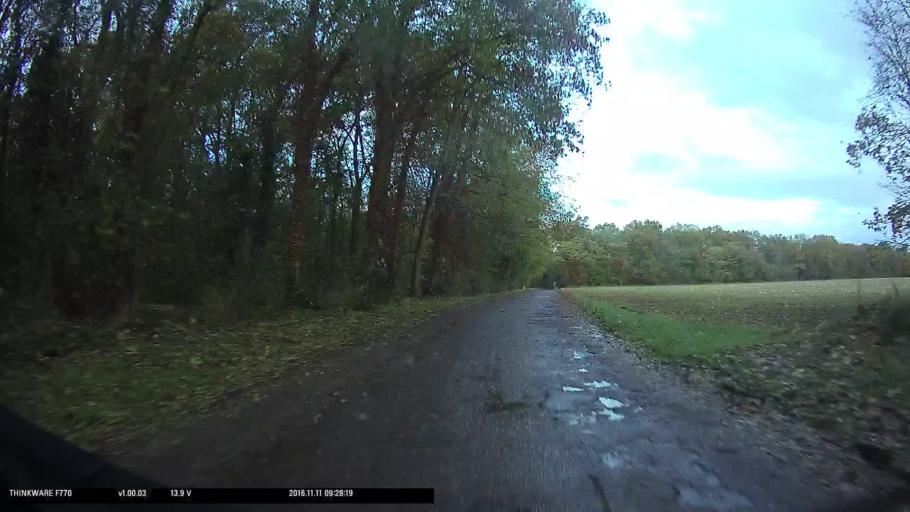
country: FR
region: Ile-de-France
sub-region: Departement du Val-d'Oise
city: Osny
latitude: 49.0709
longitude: 2.0419
